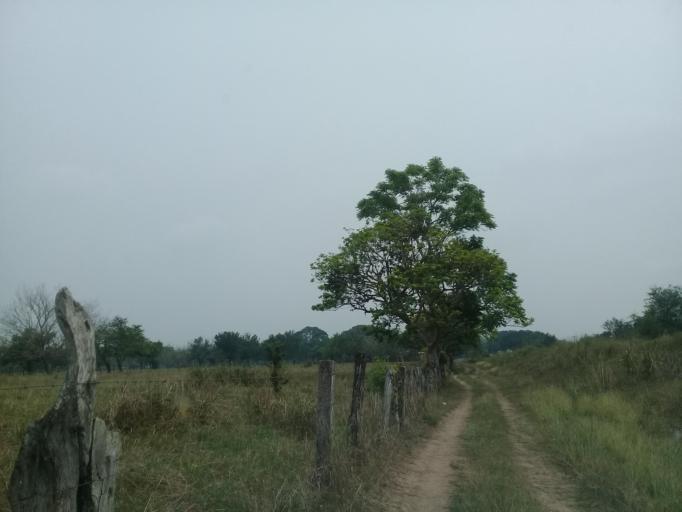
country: MX
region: Veracruz
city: Jamapa
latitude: 18.9465
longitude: -96.1979
